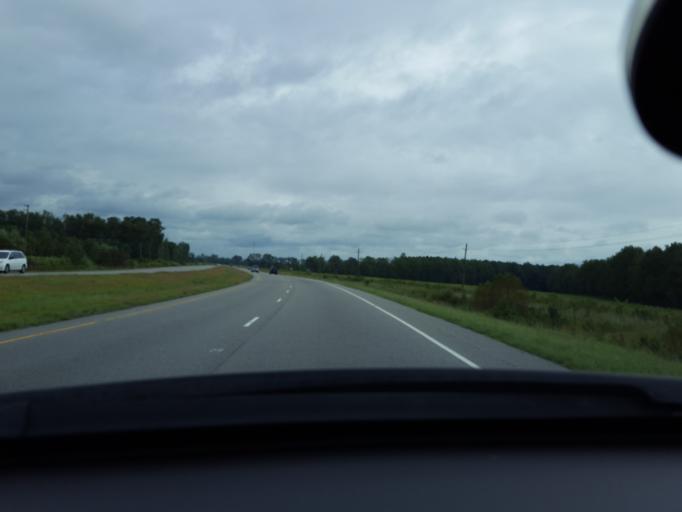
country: US
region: North Carolina
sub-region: Pitt County
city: Ayden
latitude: 35.4643
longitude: -77.4358
